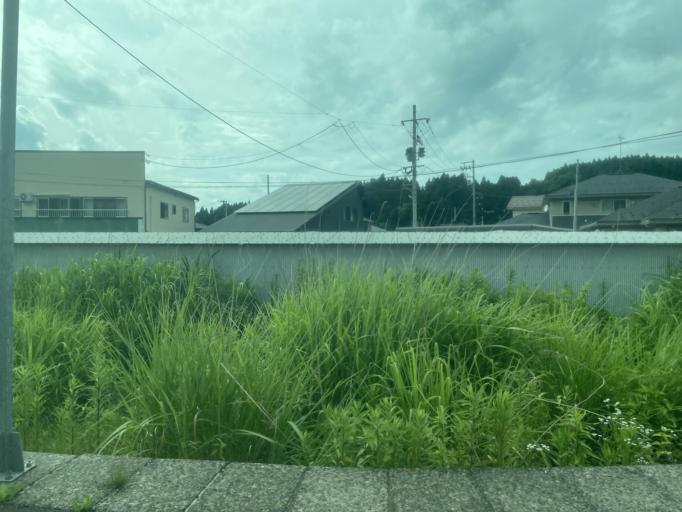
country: JP
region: Niigata
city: Kashiwazaki
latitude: 37.4593
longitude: 138.6641
